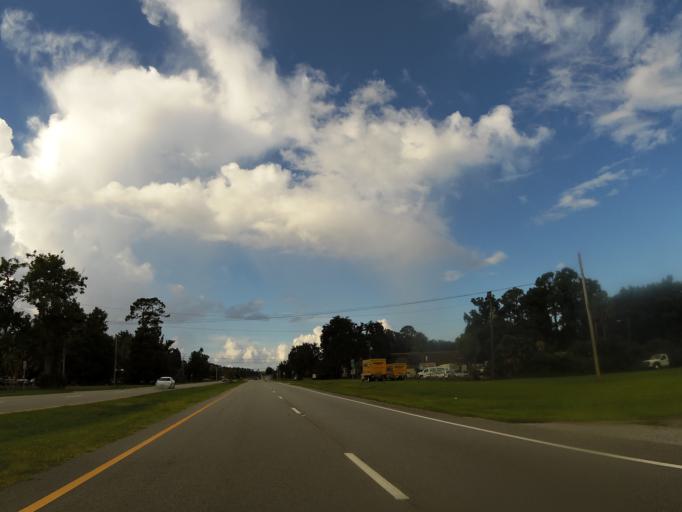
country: US
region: Georgia
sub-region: Glynn County
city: Country Club Estates
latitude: 31.1893
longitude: -81.4693
